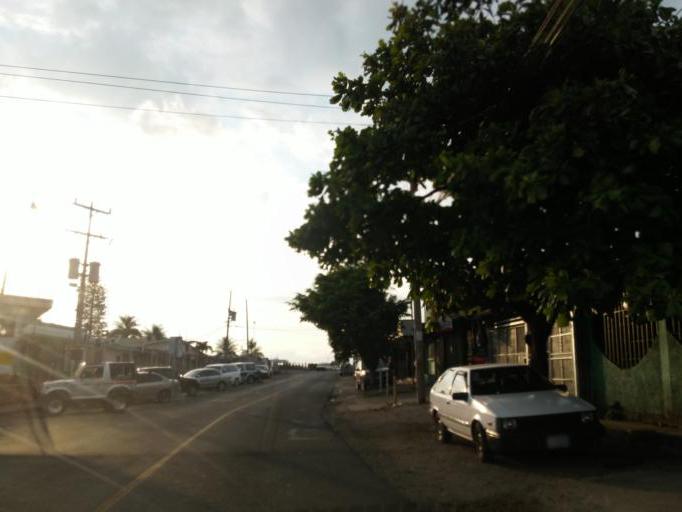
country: CR
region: Alajuela
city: Alajuela
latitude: 10.0049
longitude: -84.2272
